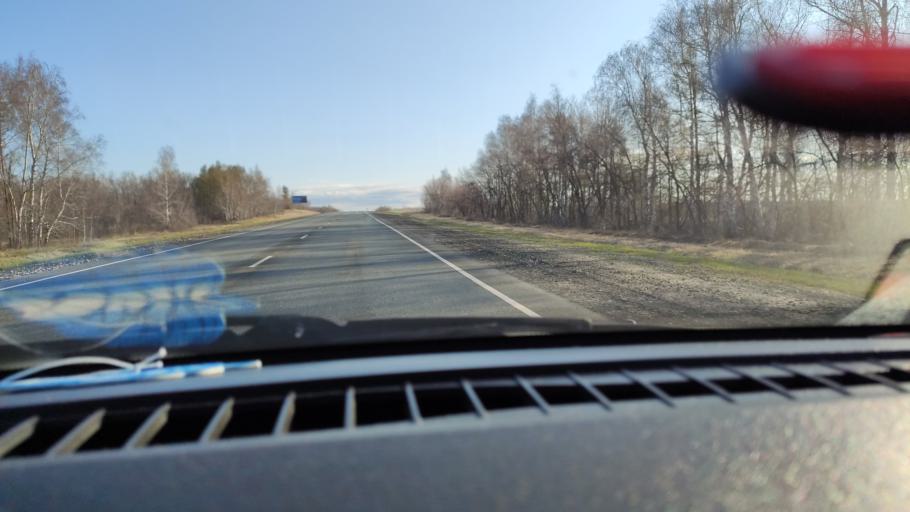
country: RU
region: Saratov
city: Khvalynsk
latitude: 52.5855
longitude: 48.1231
